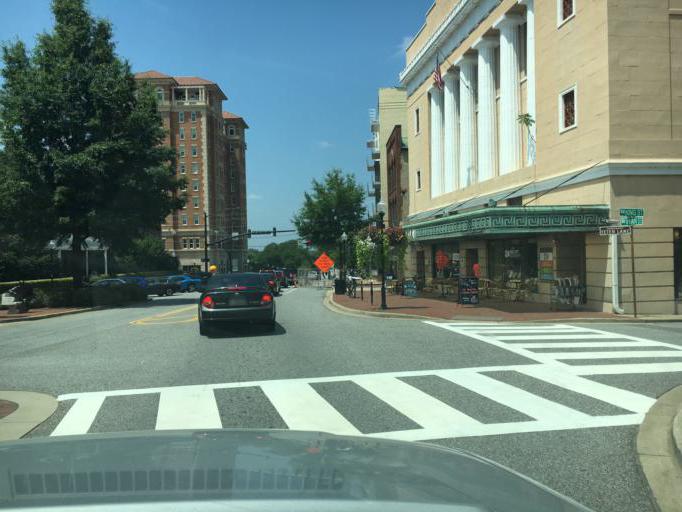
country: US
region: South Carolina
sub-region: Spartanburg County
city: Spartanburg
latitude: 34.9489
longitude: -81.9341
